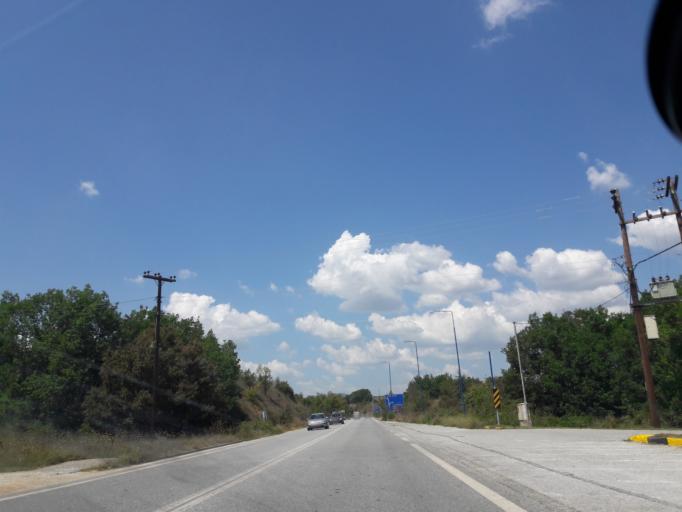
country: GR
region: Central Macedonia
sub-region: Nomos Chalkidikis
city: Galatista
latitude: 40.4629
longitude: 23.3740
